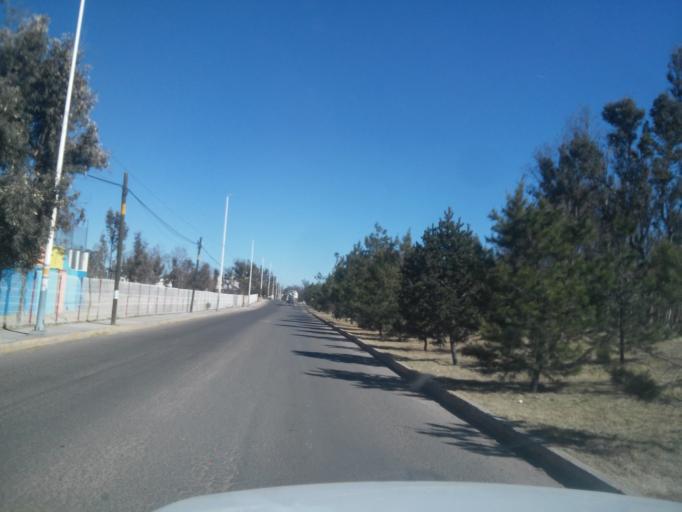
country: MX
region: Durango
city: Victoria de Durango
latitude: 24.0222
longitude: -104.6990
